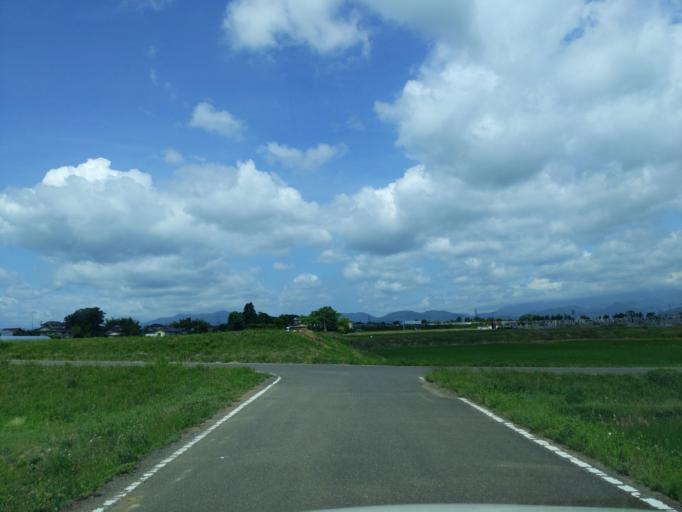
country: JP
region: Fukushima
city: Koriyama
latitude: 37.4469
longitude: 140.3576
